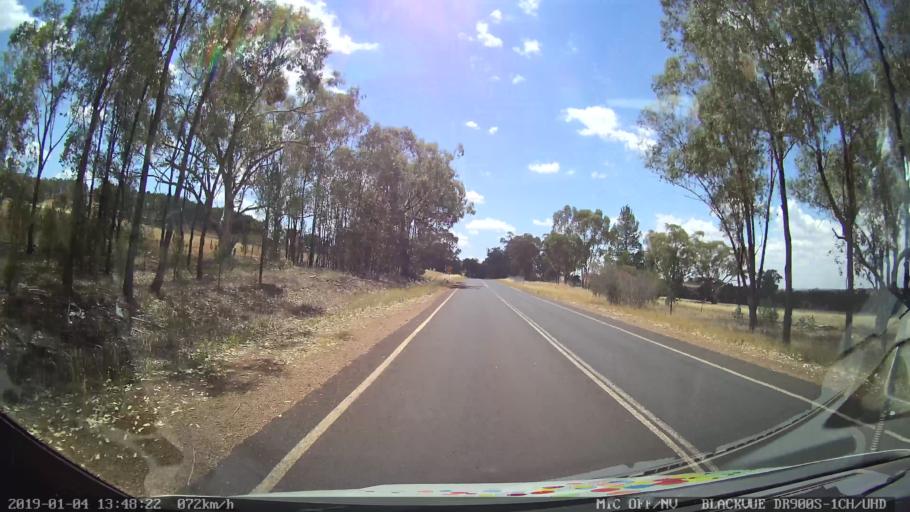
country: AU
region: New South Wales
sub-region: Dubbo Municipality
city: Dubbo
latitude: -32.4434
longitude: 148.5839
